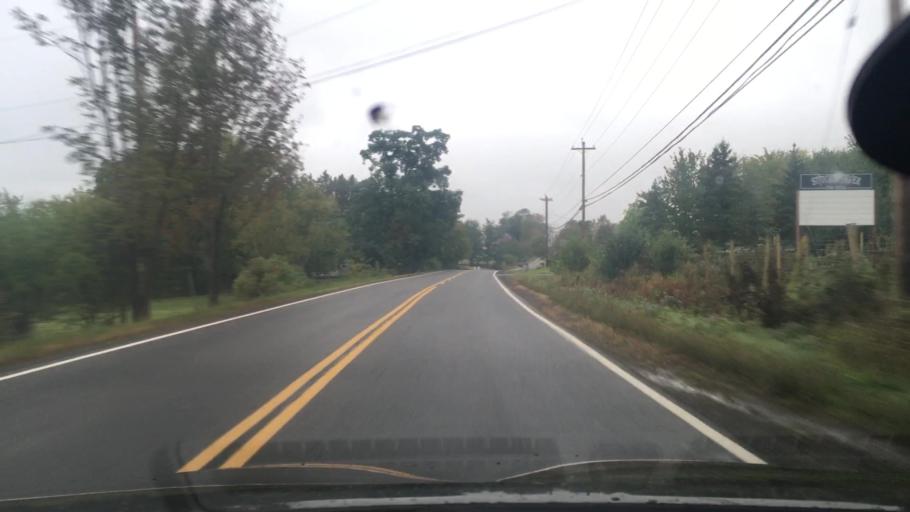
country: CA
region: Nova Scotia
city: Windsor
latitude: 44.9482
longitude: -64.1763
